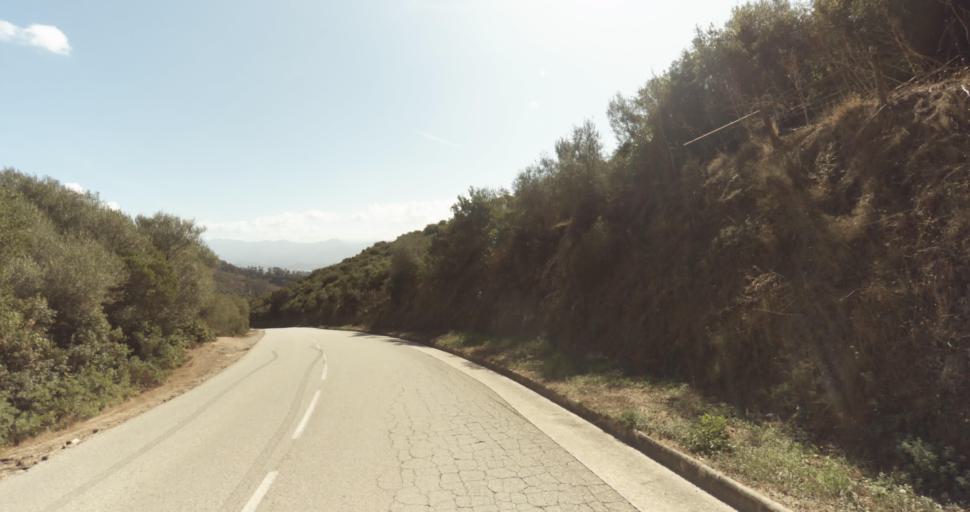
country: FR
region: Corsica
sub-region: Departement de la Corse-du-Sud
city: Ajaccio
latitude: 41.9337
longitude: 8.6804
